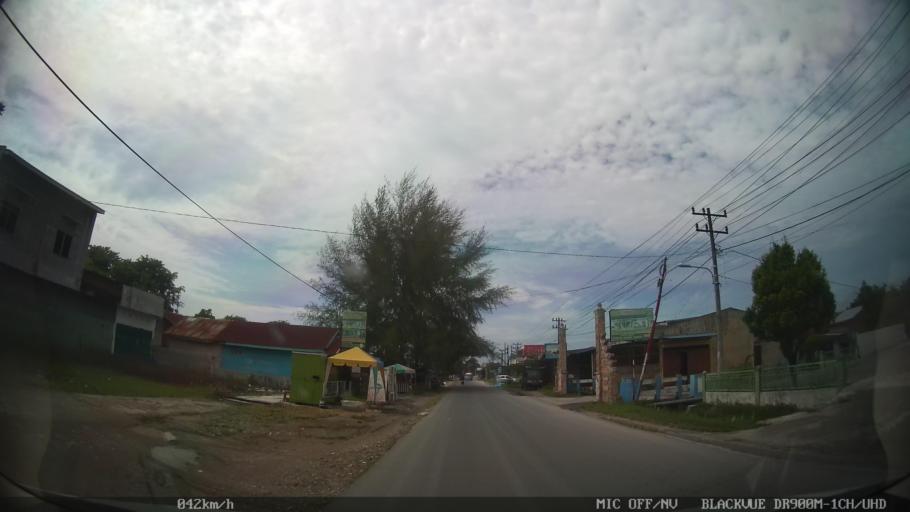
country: ID
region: North Sumatra
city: Percut
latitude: 3.6062
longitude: 98.8076
